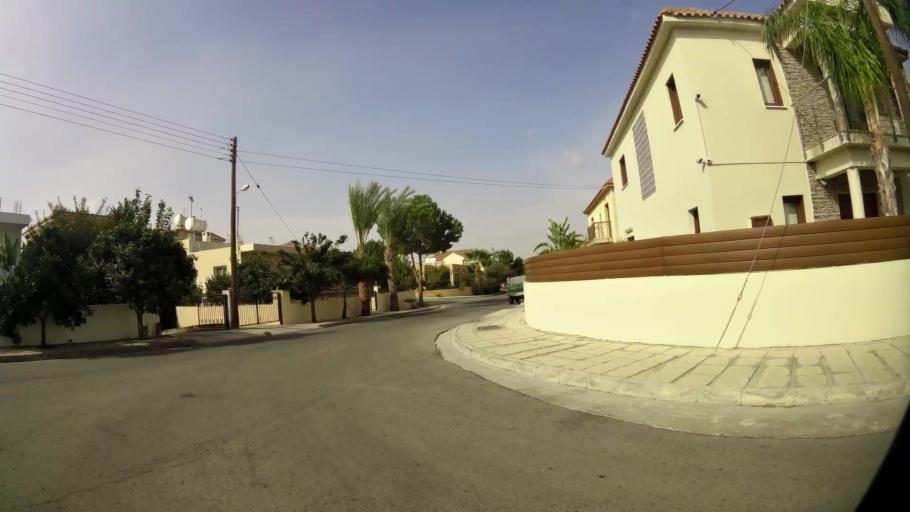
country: CY
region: Lefkosia
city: Dali
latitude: 35.0613
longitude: 33.3997
